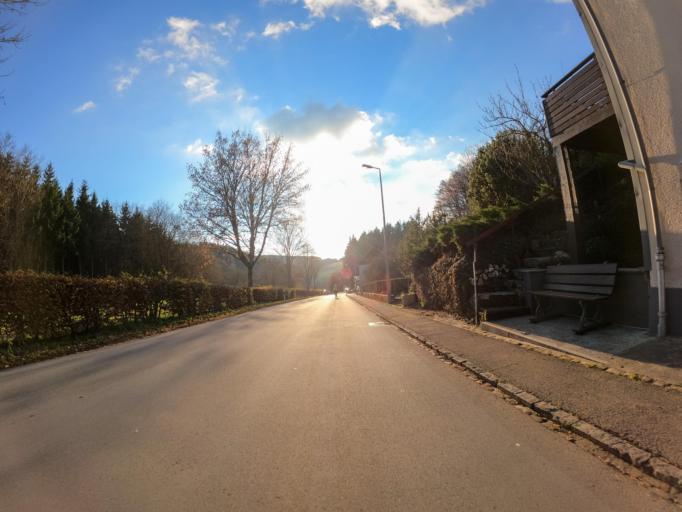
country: LU
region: Diekirch
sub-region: Canton de Wiltz
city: Bavigne
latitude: 49.9674
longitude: 5.8312
